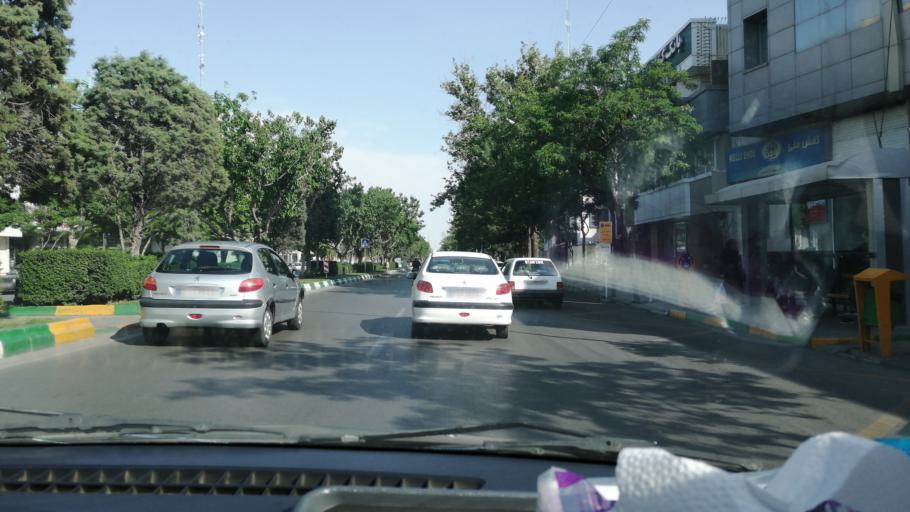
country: IR
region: Razavi Khorasan
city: Mashhad
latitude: 36.3142
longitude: 59.5611
